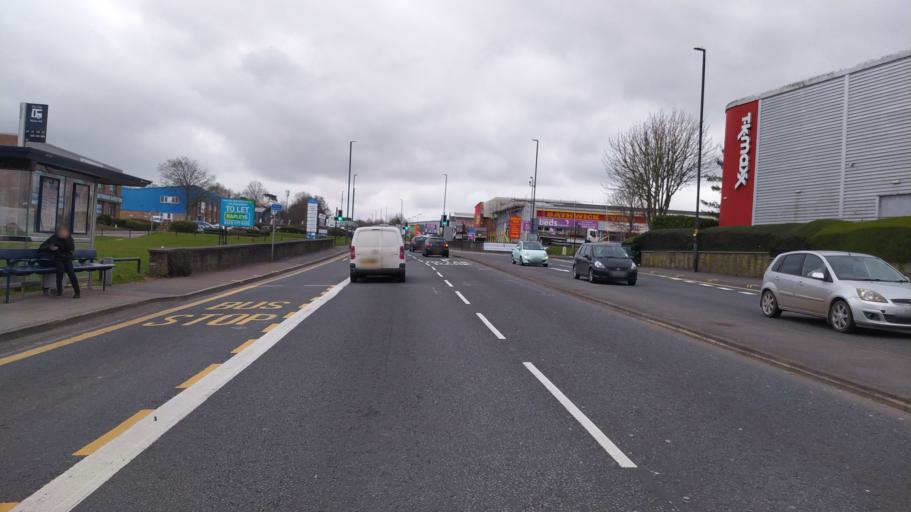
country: GB
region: England
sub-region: Bath and North East Somerset
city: Whitchurch
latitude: 51.4305
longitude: -2.5433
